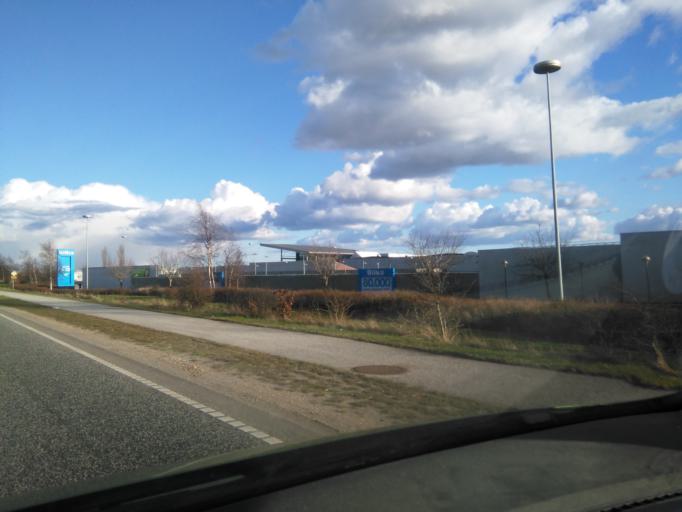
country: DK
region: Central Jutland
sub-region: Arhus Kommune
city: Stavtrup
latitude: 56.1840
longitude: 10.1048
